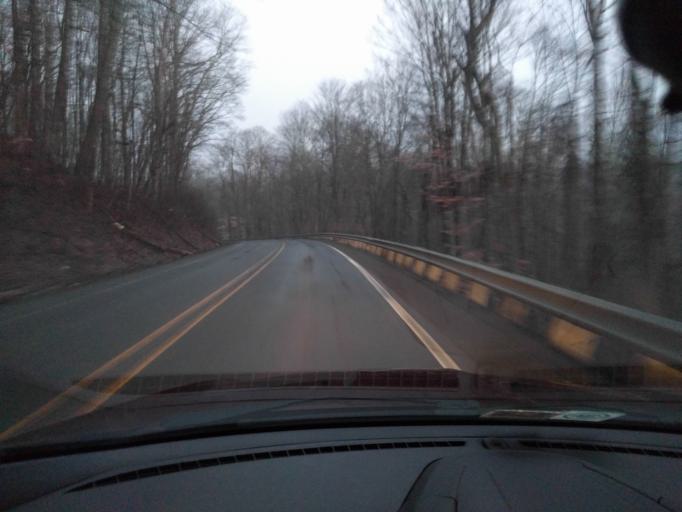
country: US
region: West Virginia
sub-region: Greenbrier County
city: Rainelle
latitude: 37.9826
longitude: -80.8333
